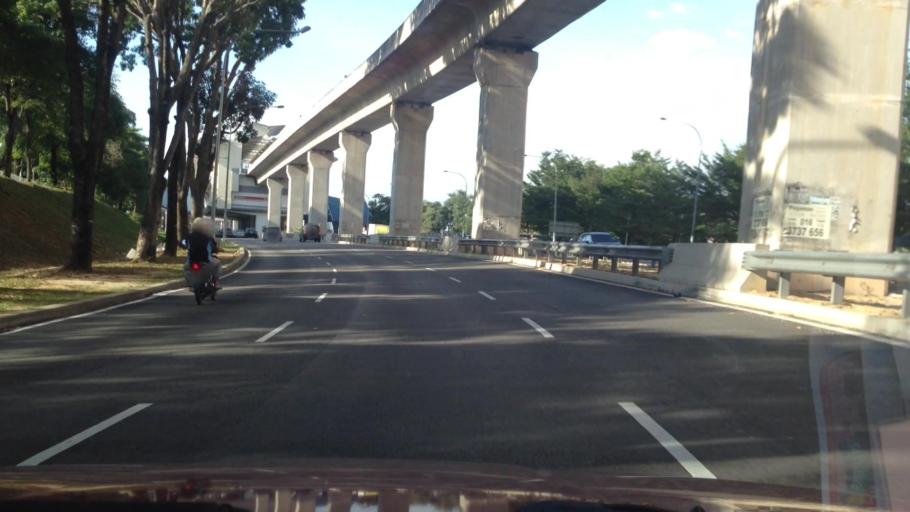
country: MY
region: Selangor
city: Subang Jaya
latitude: 3.0327
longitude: 101.5880
